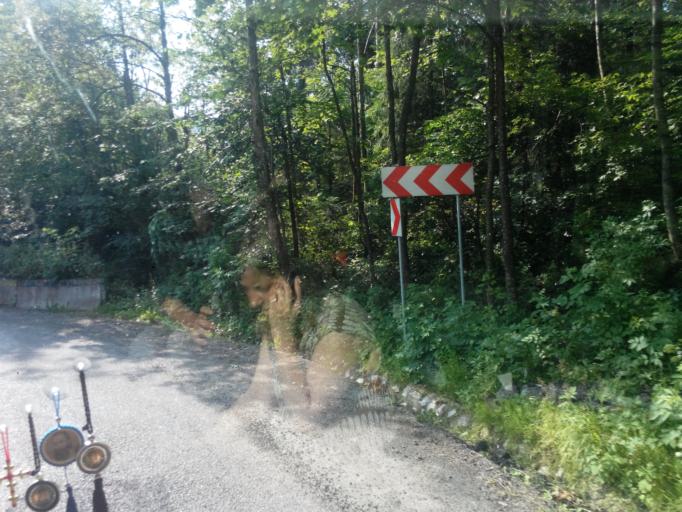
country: RO
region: Brasov
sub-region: Oras Predeal
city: Predeal
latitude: 45.5192
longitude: 25.5083
